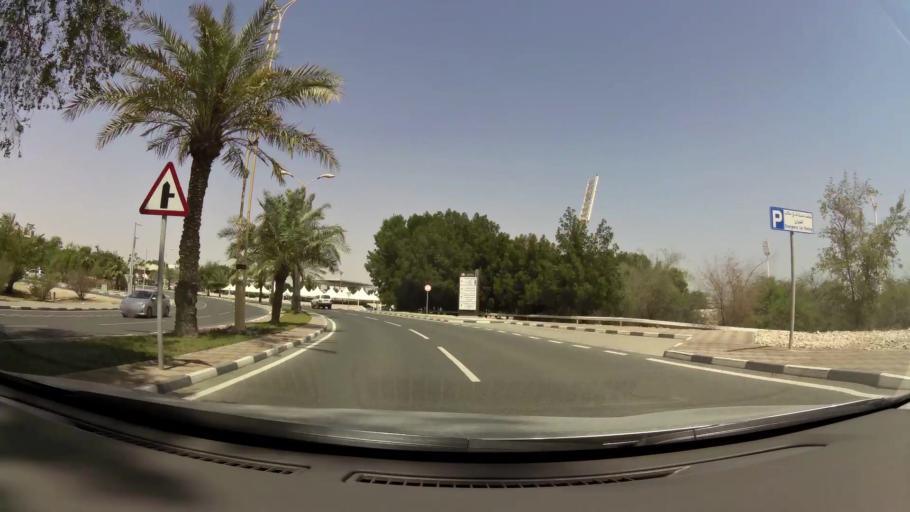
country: QA
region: Baladiyat ad Dawhah
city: Doha
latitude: 25.3733
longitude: 51.4952
